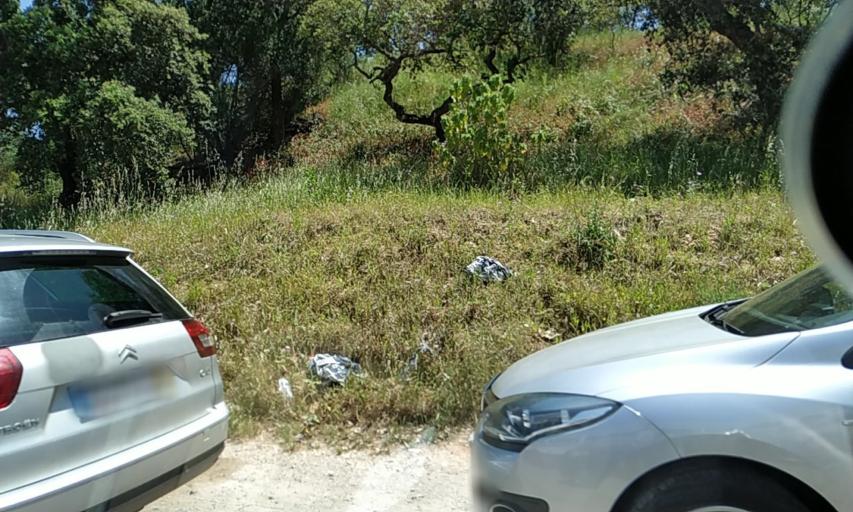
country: PT
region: Setubal
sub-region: Setubal
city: Setubal
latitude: 38.5381
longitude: -8.8716
